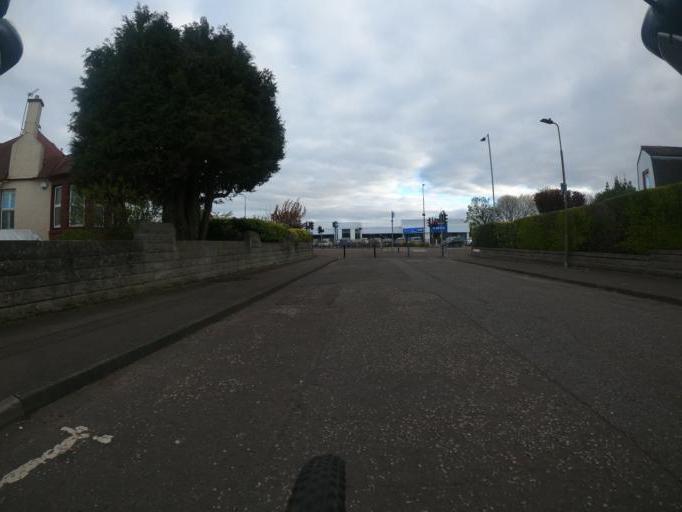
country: GB
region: Scotland
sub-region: Edinburgh
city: Currie
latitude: 55.9414
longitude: -3.3065
